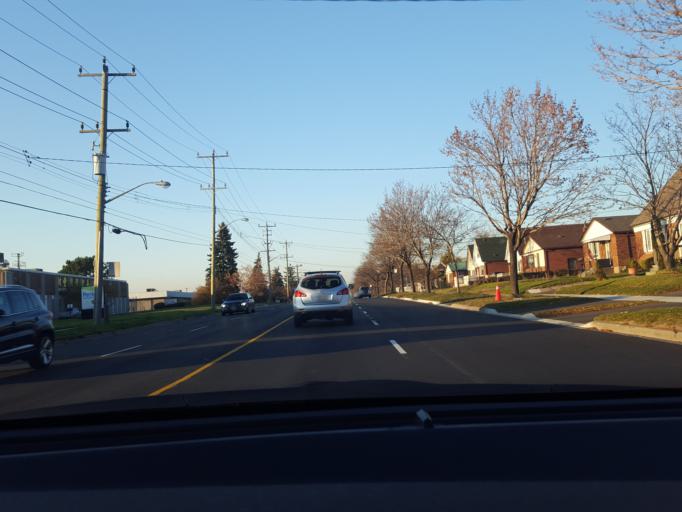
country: CA
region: Ontario
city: Scarborough
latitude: 43.7525
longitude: -79.2868
